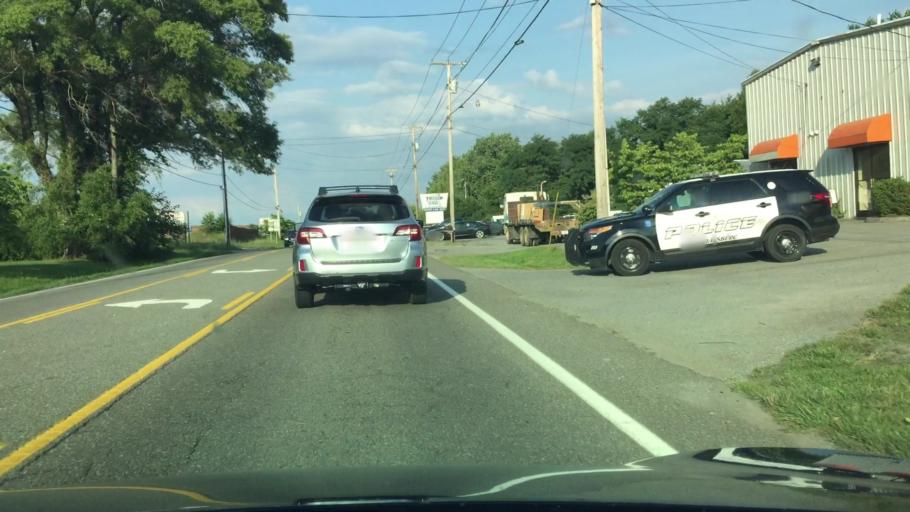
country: US
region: Virginia
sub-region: Montgomery County
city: Christiansburg
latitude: 37.1275
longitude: -80.4241
